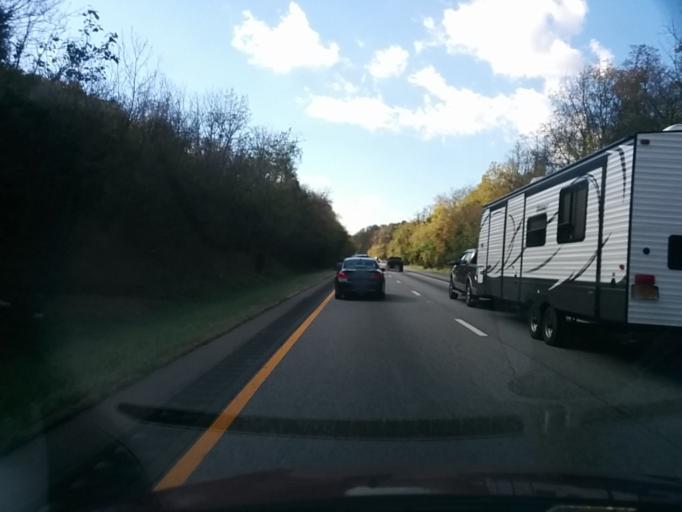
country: US
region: Virginia
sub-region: Botetourt County
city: Daleville
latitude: 37.4373
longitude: -79.8696
